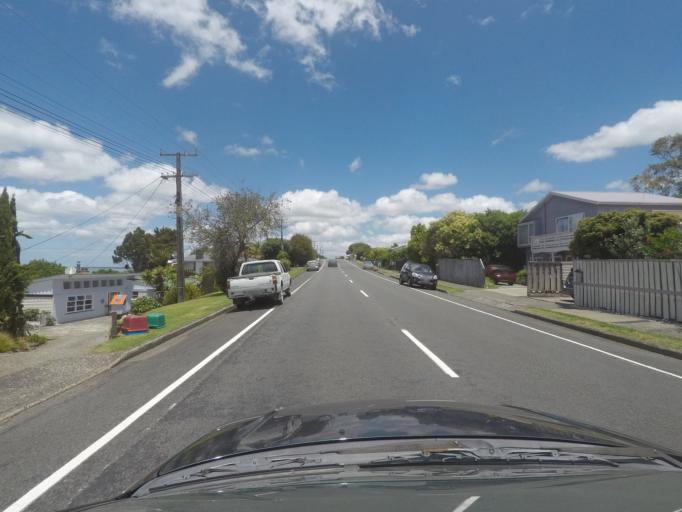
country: NZ
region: Northland
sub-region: Whangarei
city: Whangarei
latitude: -35.7623
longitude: 174.3671
